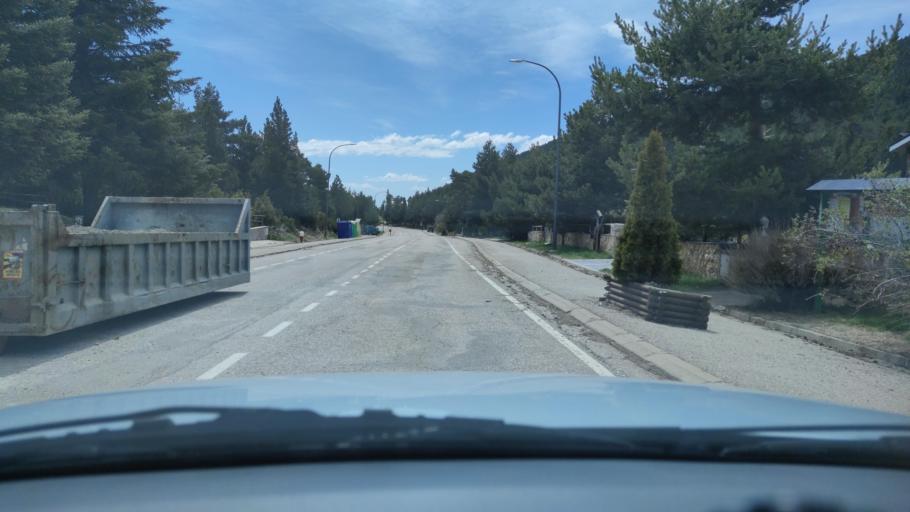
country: ES
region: Catalonia
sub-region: Provincia de Lleida
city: Gosol
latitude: 42.1716
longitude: 1.5687
